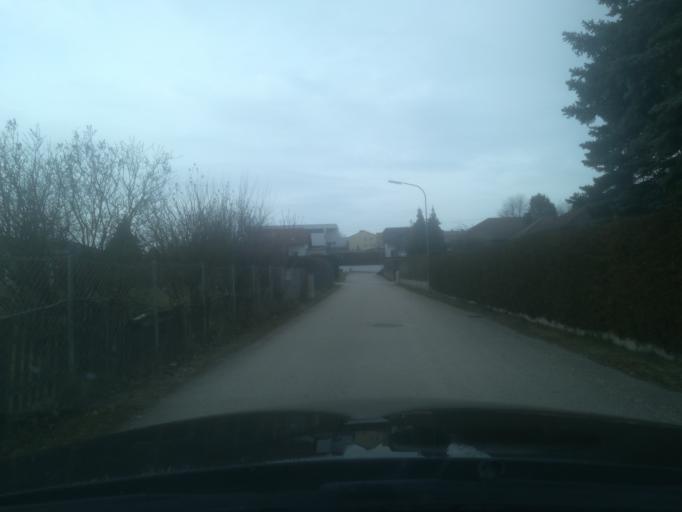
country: AT
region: Upper Austria
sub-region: Politischer Bezirk Linz-Land
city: Horsching
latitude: 48.2199
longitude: 14.1856
